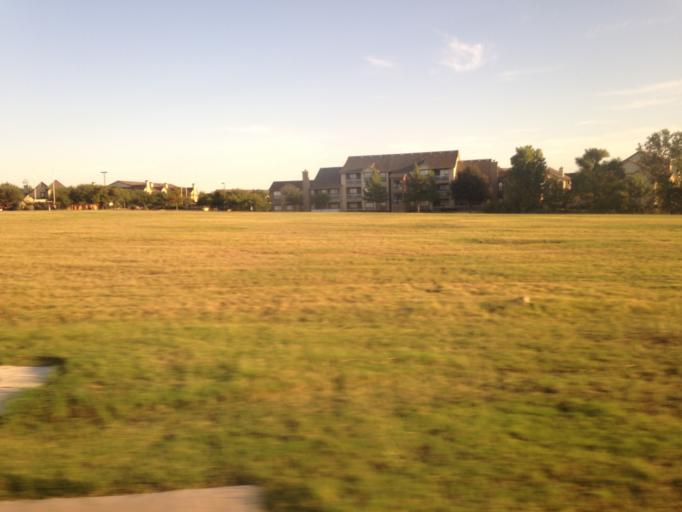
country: US
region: Texas
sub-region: Tarrant County
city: Watauga
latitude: 32.8401
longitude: -97.2844
